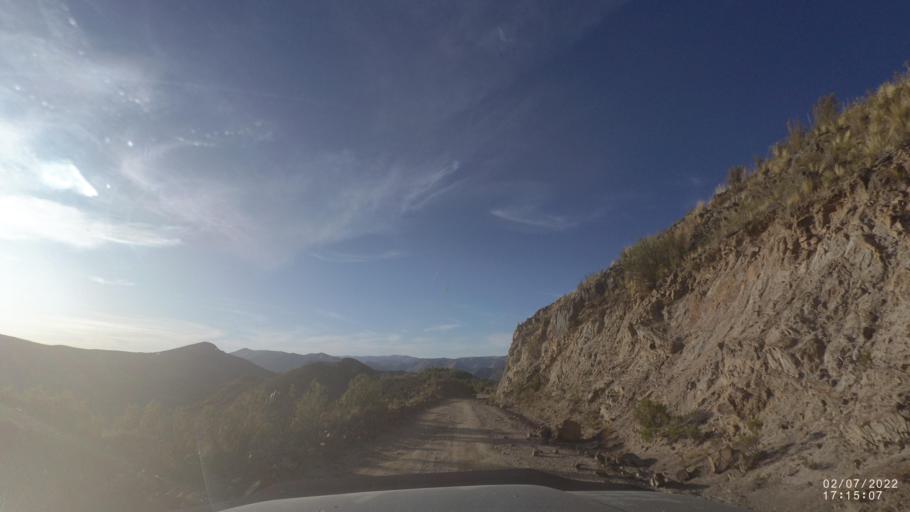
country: BO
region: Cochabamba
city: Irpa Irpa
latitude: -17.8768
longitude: -66.5834
